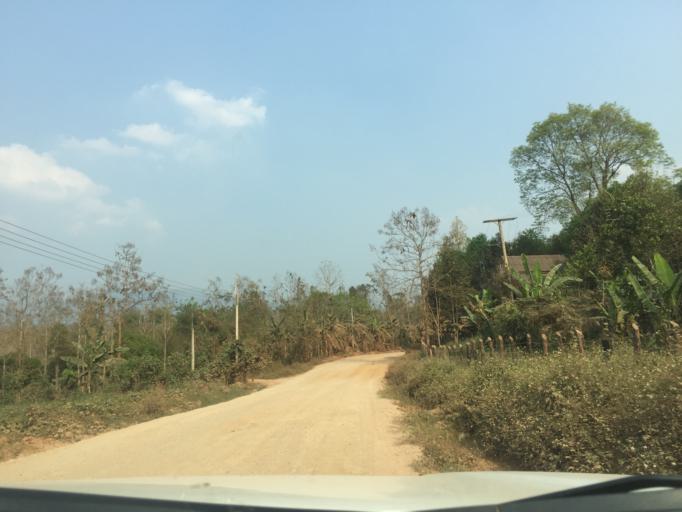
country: LA
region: Xiagnabouli
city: Sainyabuli
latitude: 19.2143
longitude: 101.6920
